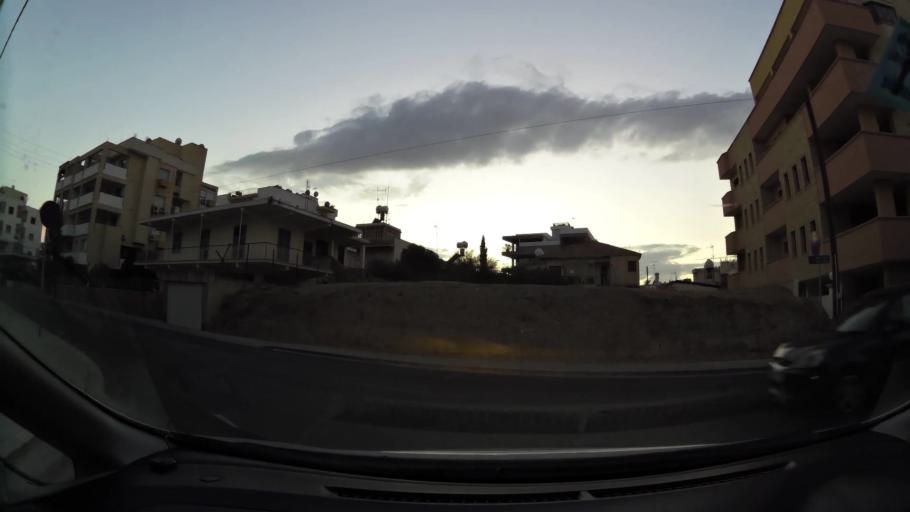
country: CY
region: Lefkosia
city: Nicosia
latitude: 35.1658
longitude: 33.3750
